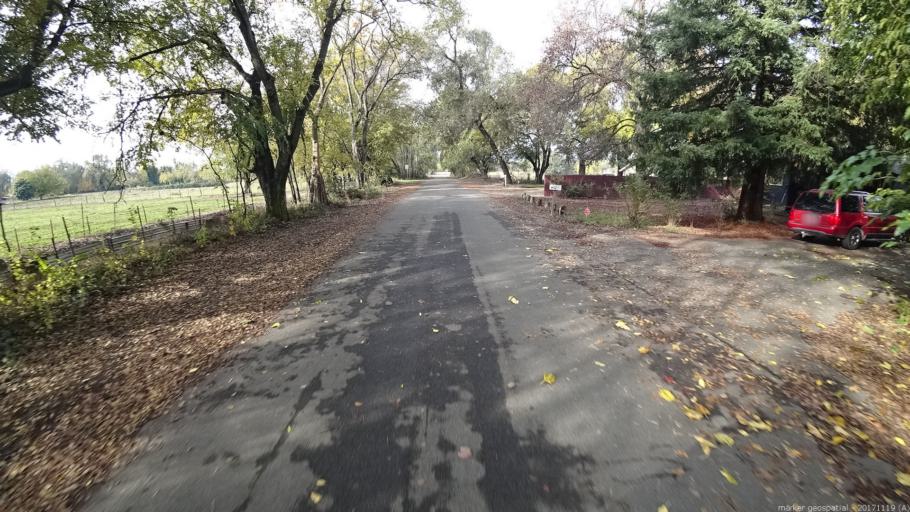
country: US
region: California
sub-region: Shasta County
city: Redding
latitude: 40.5176
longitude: -122.3496
